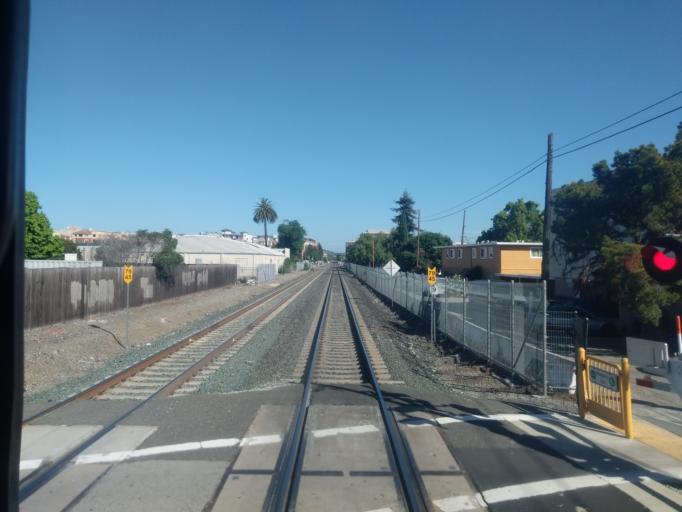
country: US
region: California
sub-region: San Mateo County
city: Redwood City
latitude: 37.4806
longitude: -122.2228
